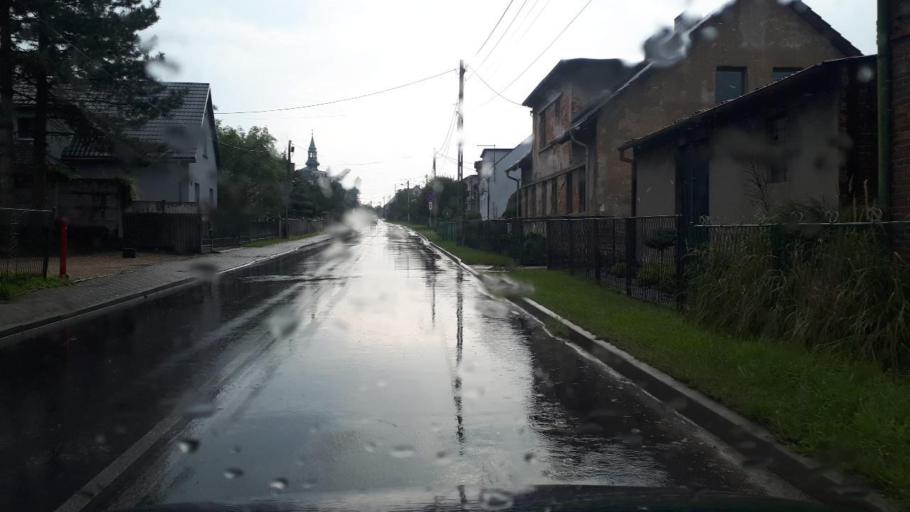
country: PL
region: Silesian Voivodeship
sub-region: Powiat gliwicki
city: Wielowies
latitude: 50.5112
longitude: 18.6202
